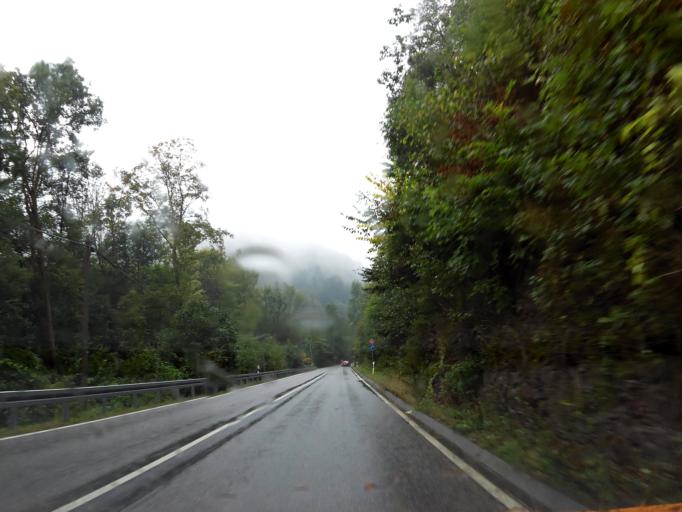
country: DE
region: Thuringia
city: Ilfeld
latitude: 51.6052
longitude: 10.7898
